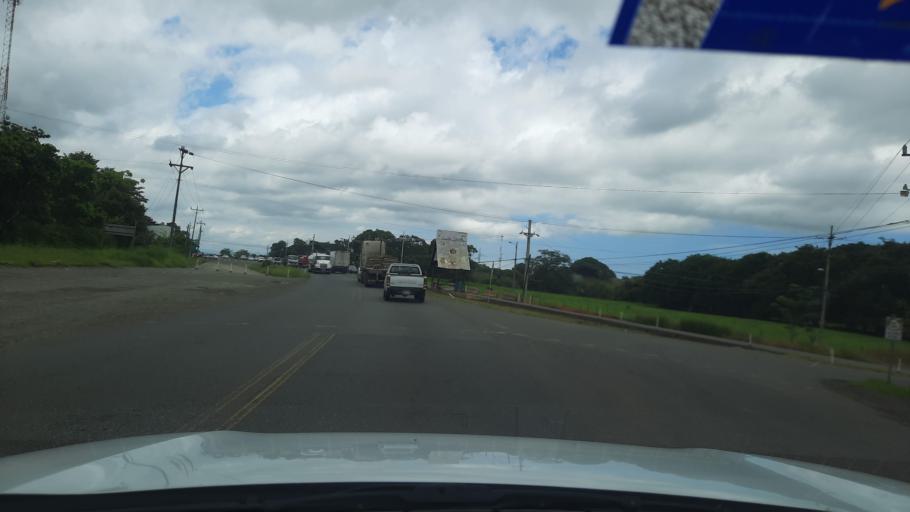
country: CR
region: Puntarenas
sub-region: Canton Central de Puntarenas
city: Puntarenas
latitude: 10.1133
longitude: -84.8932
